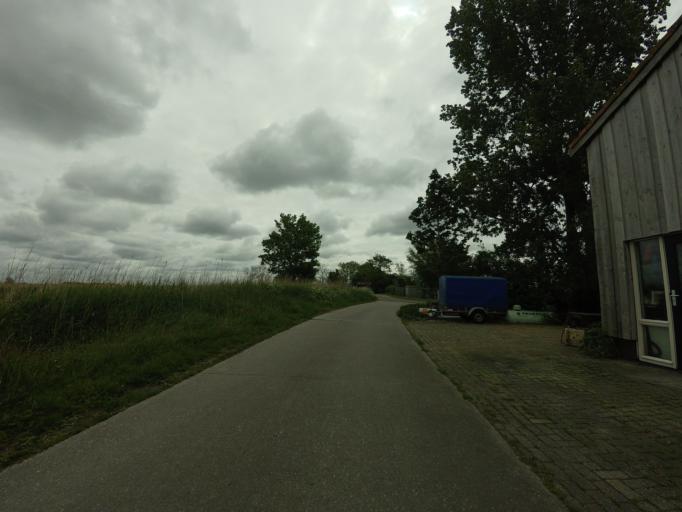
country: NL
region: Friesland
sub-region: Sudwest Fryslan
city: Workum
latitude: 53.0018
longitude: 5.4647
